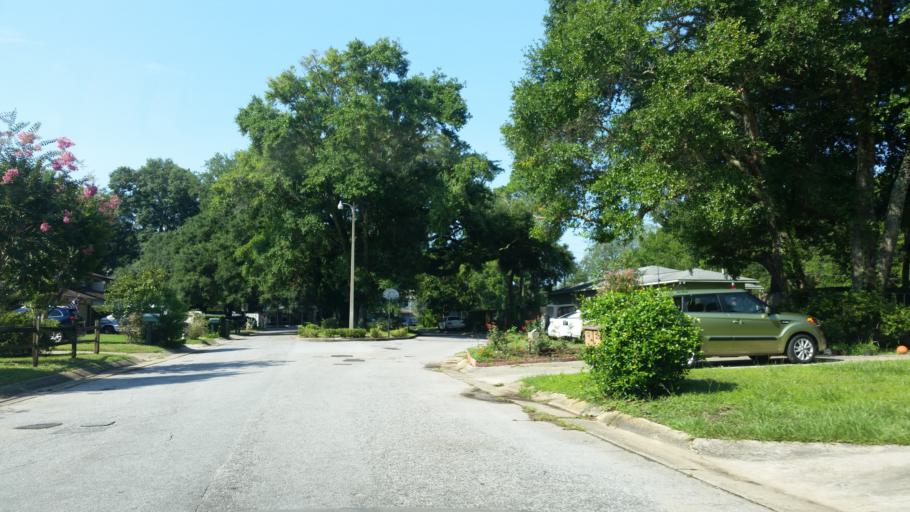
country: US
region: Florida
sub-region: Escambia County
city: Ferry Pass
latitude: 30.4990
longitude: -87.1722
